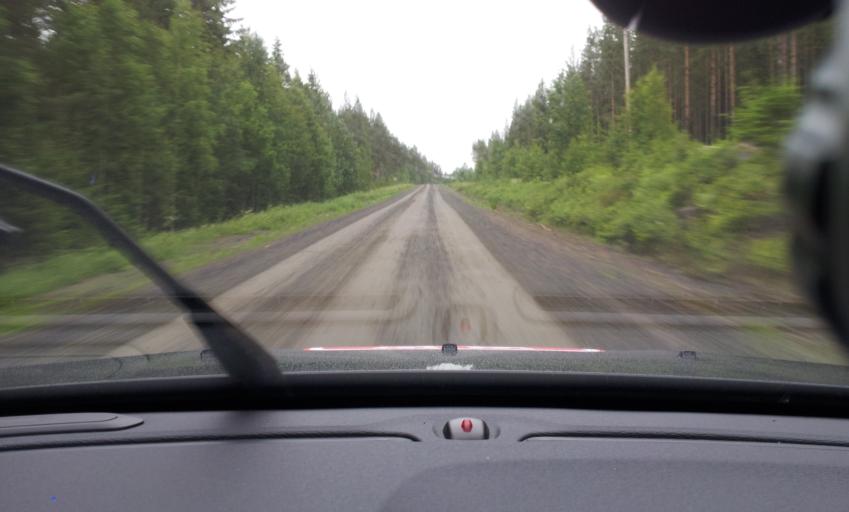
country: SE
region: Jaemtland
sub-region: Ragunda Kommun
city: Hammarstrand
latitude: 63.1440
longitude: 16.2199
